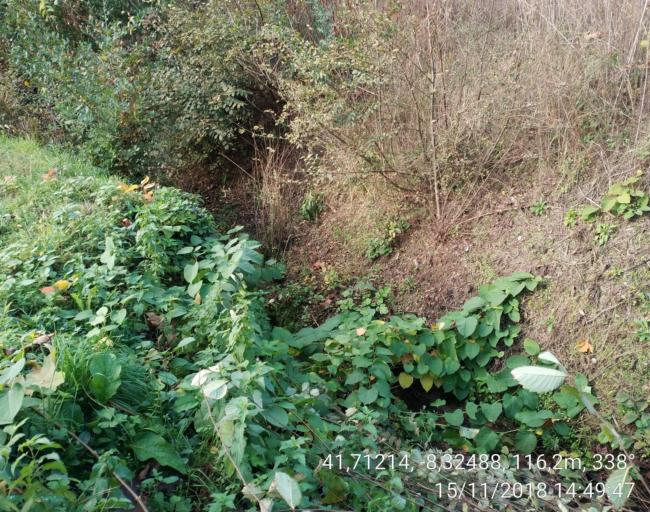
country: PT
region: Braga
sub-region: Terras de Bouro
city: Terras de Bouro
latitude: 41.7121
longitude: -8.3249
